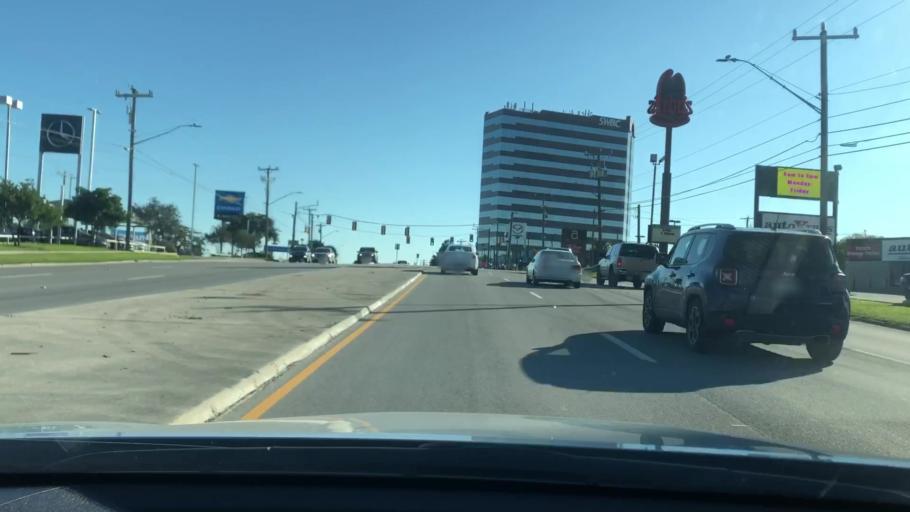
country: US
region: Texas
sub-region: Bexar County
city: Castle Hills
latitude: 29.5276
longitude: -98.4983
